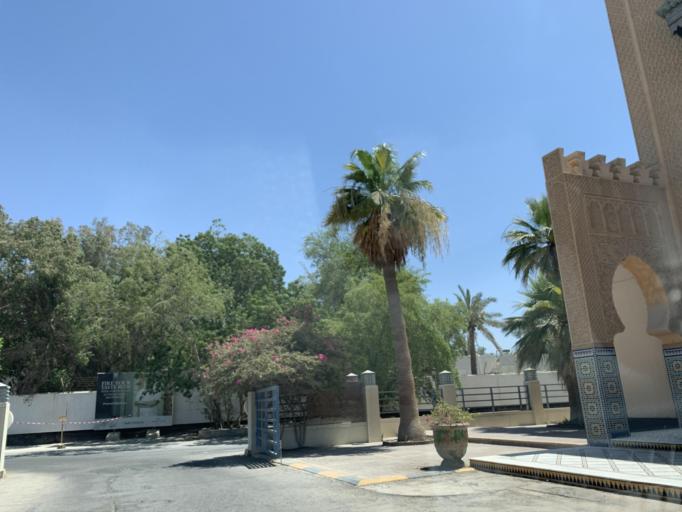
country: BH
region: Manama
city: Jidd Hafs
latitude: 26.2208
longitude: 50.4895
